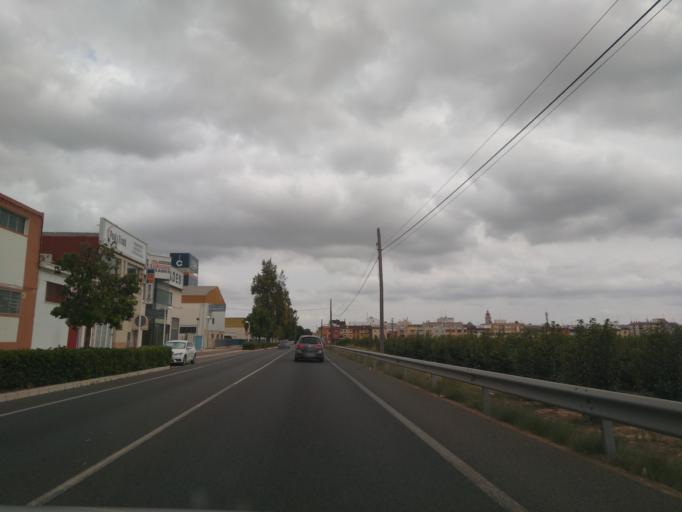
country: ES
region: Valencia
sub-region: Provincia de Valencia
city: L'Alcudia
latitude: 39.2045
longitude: -0.5079
